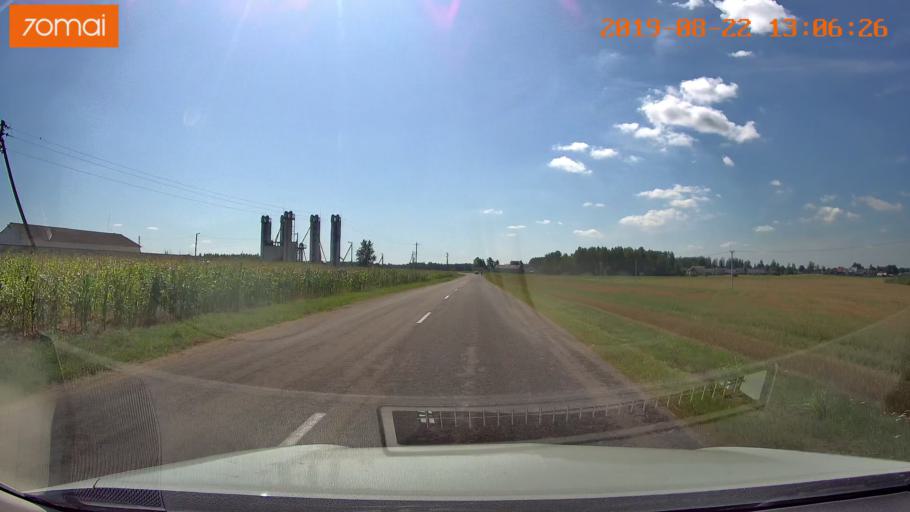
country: BY
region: Minsk
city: Prawdzinski
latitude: 53.3471
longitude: 27.8384
